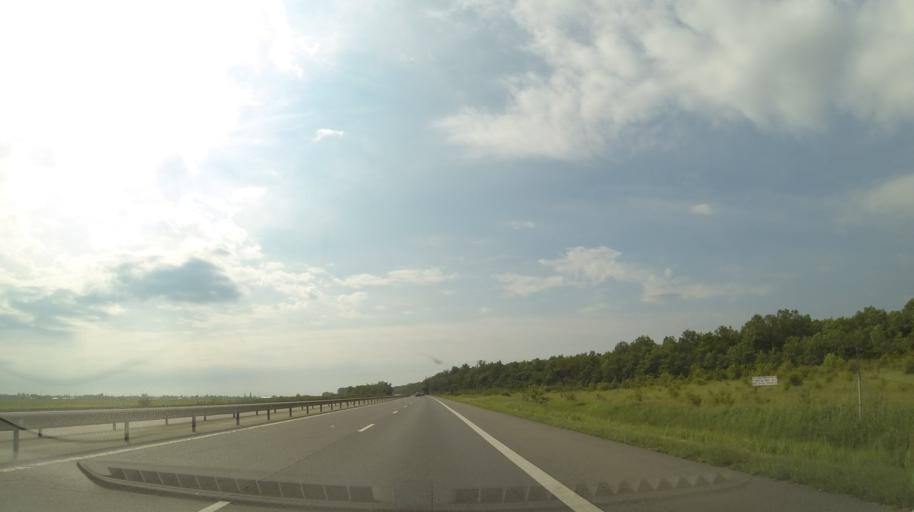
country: RO
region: Dambovita
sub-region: Comuna Corbii Mari
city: Grozavesti
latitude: 44.5878
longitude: 25.4638
